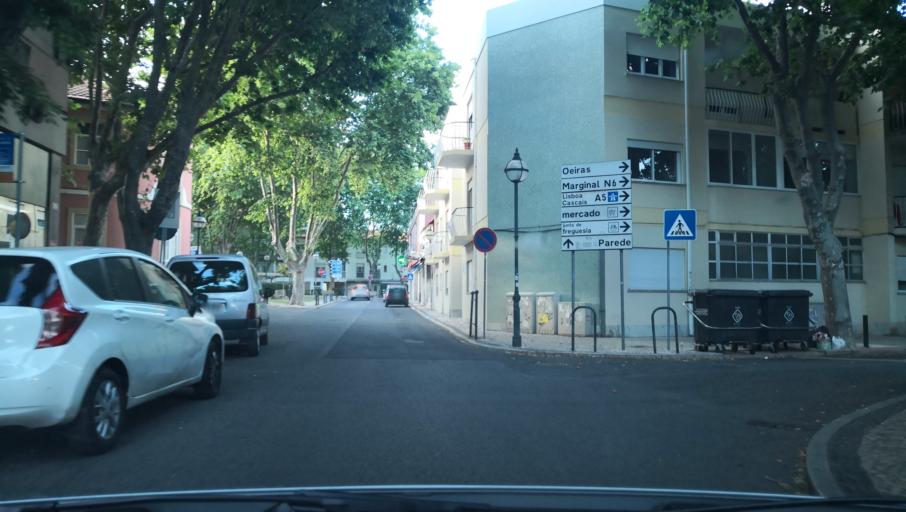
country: PT
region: Lisbon
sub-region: Oeiras
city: Carcavelos
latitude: 38.6895
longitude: -9.3354
